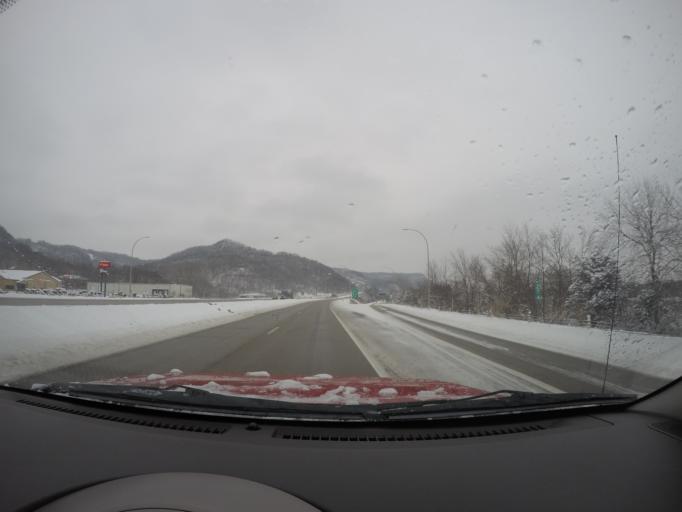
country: US
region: Minnesota
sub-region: Houston County
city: La Crescent
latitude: 43.8844
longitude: -91.3346
